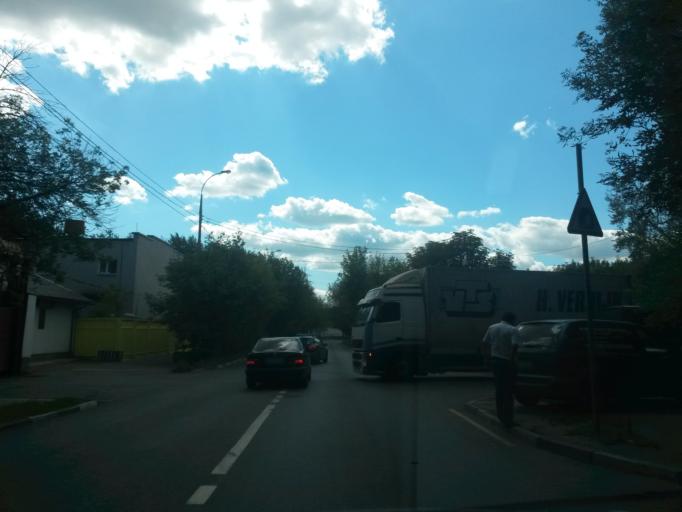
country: RU
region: Moscow
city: Mar'ino
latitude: 55.6591
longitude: 37.7174
